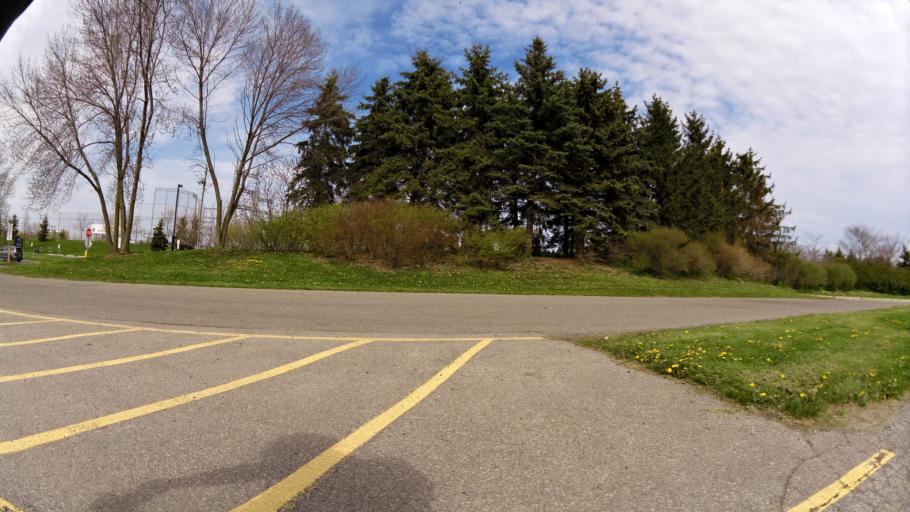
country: CA
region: Ontario
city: Etobicoke
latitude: 43.5717
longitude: -79.5572
